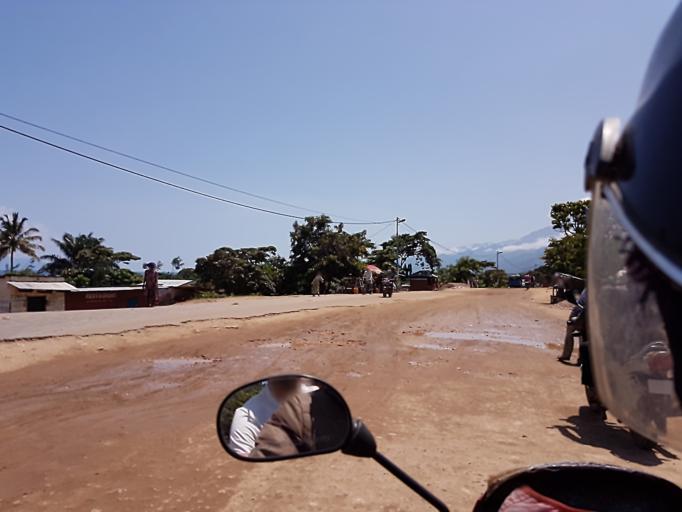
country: CD
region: South Kivu
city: Uvira
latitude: -3.3551
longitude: 29.1542
